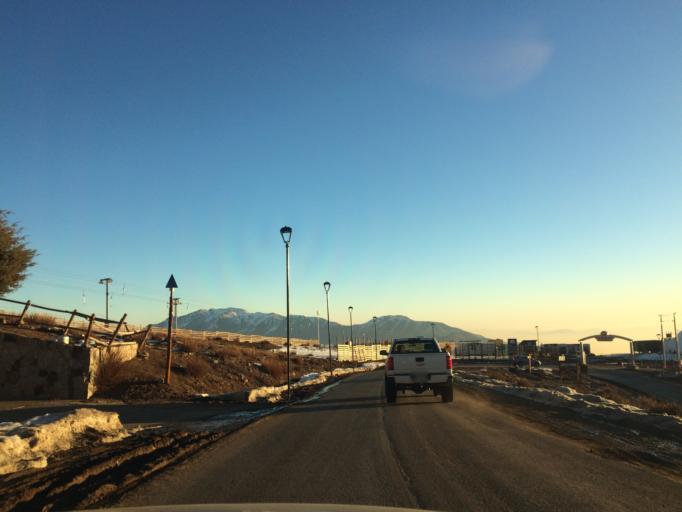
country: CL
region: Santiago Metropolitan
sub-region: Provincia de Santiago
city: Villa Presidente Frei, Nunoa, Santiago, Chile
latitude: -33.3499
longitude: -70.2957
